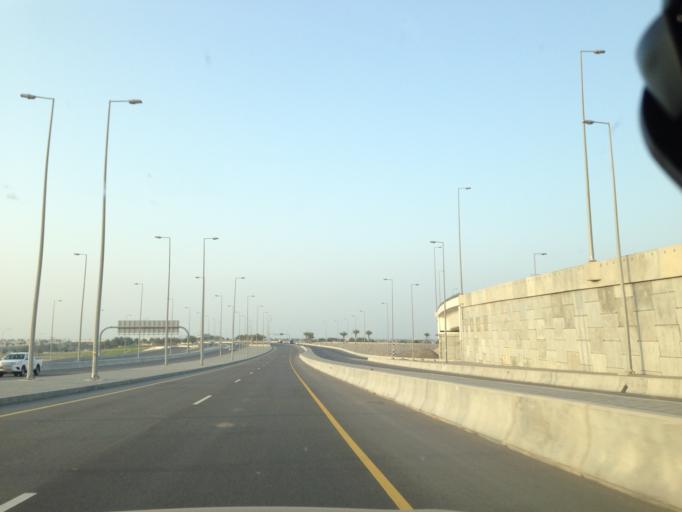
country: OM
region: Muhafazat Masqat
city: Bawshar
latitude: 23.5870
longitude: 58.3327
